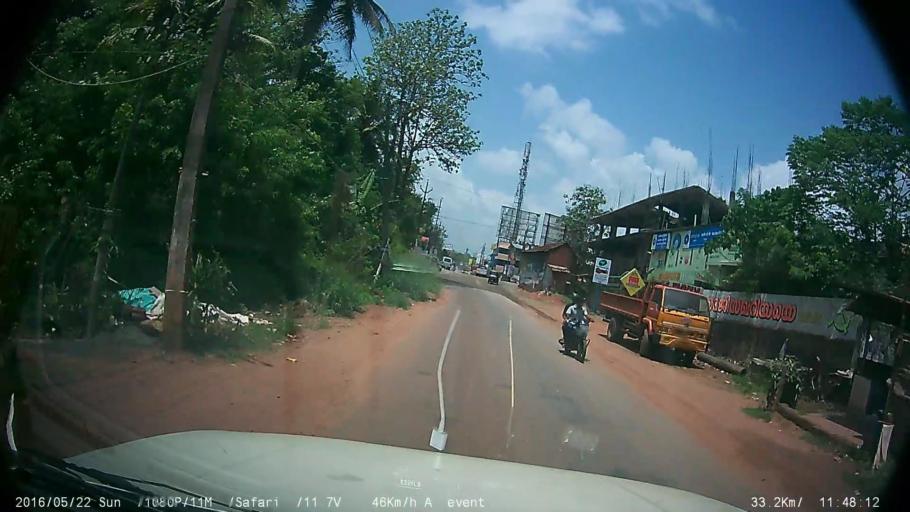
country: IN
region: Kerala
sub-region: Kottayam
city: Kottayam
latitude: 9.5258
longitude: 76.5246
